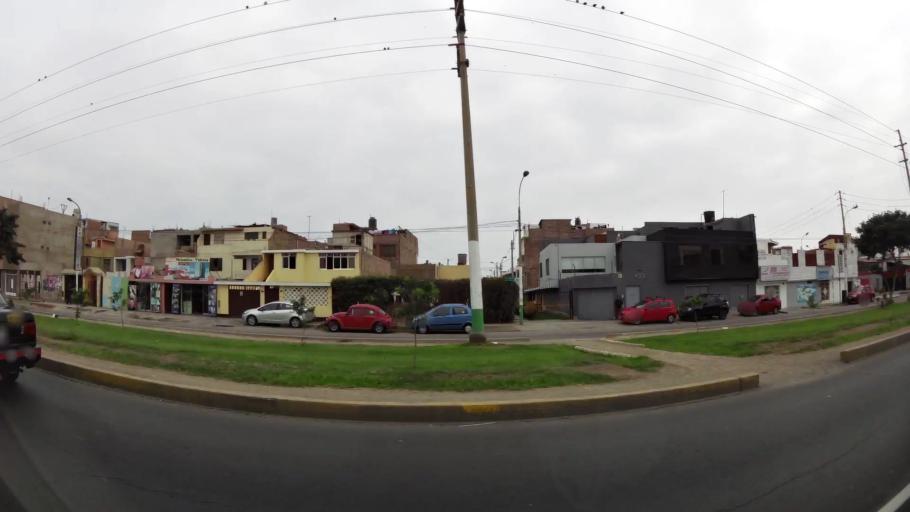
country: PE
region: Callao
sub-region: Callao
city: Callao
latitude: -12.0683
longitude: -77.1146
